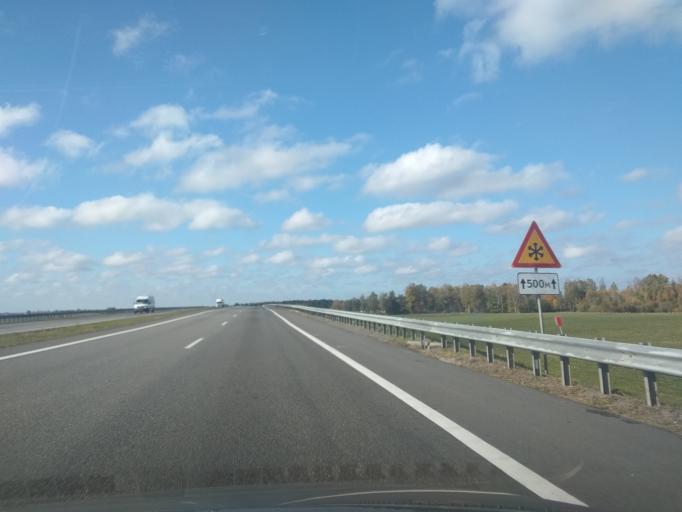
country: BY
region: Minsk
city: Dzyarzhynsk
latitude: 53.6594
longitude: 27.1069
